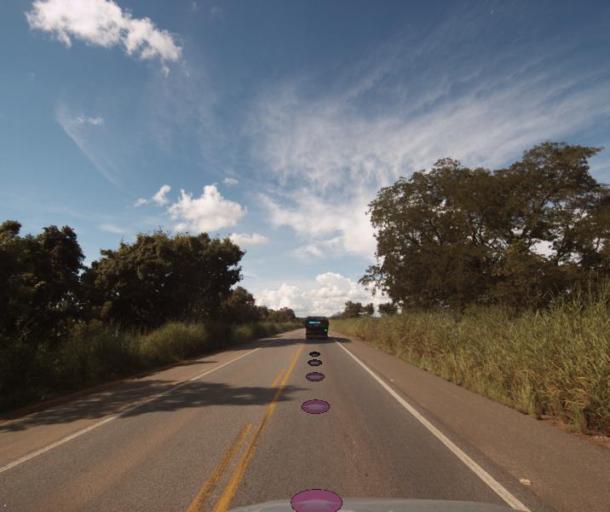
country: BR
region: Goias
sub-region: Porangatu
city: Porangatu
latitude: -13.0773
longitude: -49.1884
